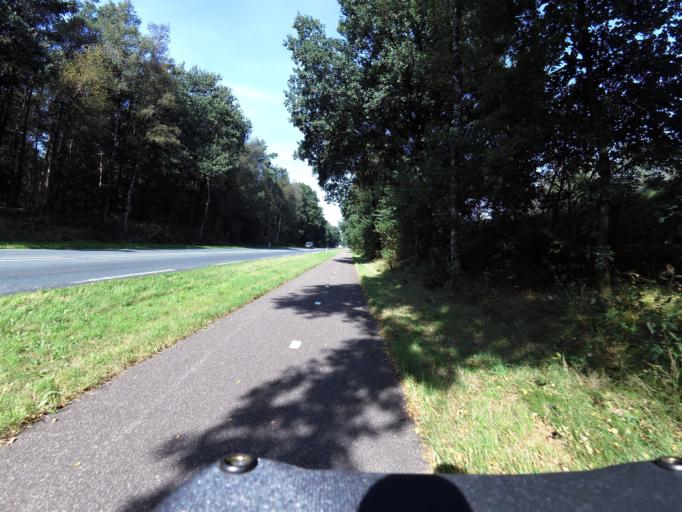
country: NL
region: Gelderland
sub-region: Gemeente Apeldoorn
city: Uddel
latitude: 52.2269
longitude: 5.7757
